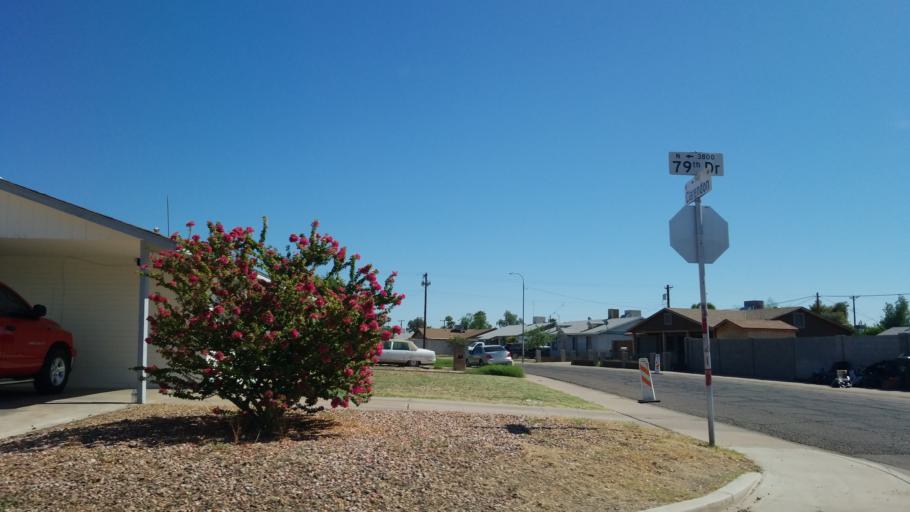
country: US
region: Arizona
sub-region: Maricopa County
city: Tolleson
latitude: 33.4909
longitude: -112.2302
